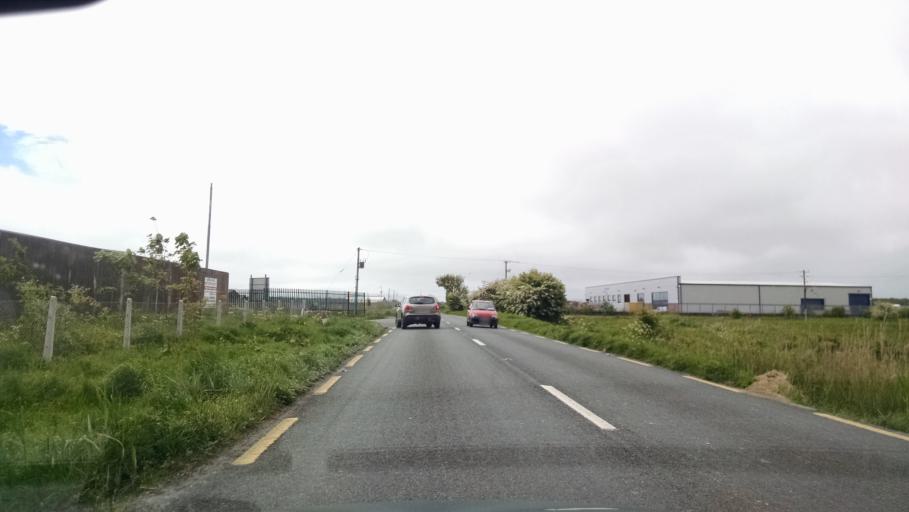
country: IE
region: Connaught
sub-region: County Galway
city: Gaillimh
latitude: 53.3300
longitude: -9.0206
